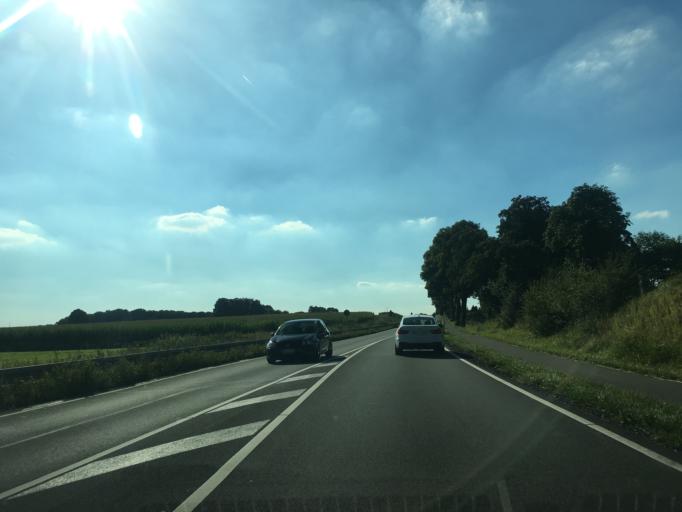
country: DE
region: North Rhine-Westphalia
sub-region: Regierungsbezirk Munster
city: Warendorf
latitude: 51.9581
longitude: 7.9288
